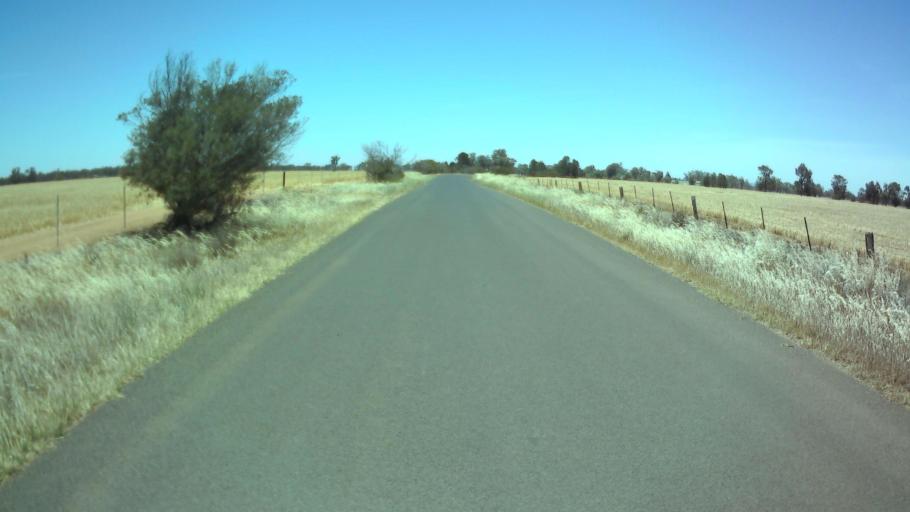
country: AU
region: New South Wales
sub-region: Weddin
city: Grenfell
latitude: -34.0539
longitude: 147.7811
